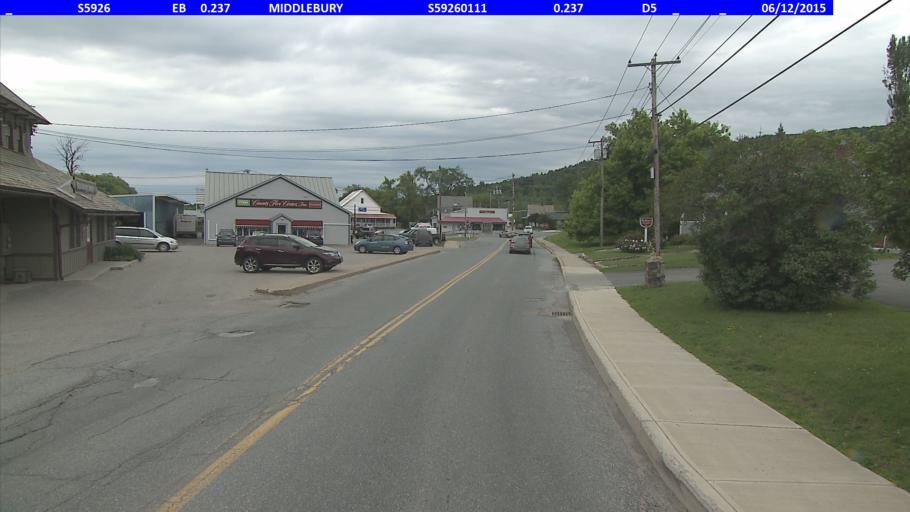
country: US
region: Vermont
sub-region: Addison County
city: Middlebury (village)
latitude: 44.0174
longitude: -73.1694
